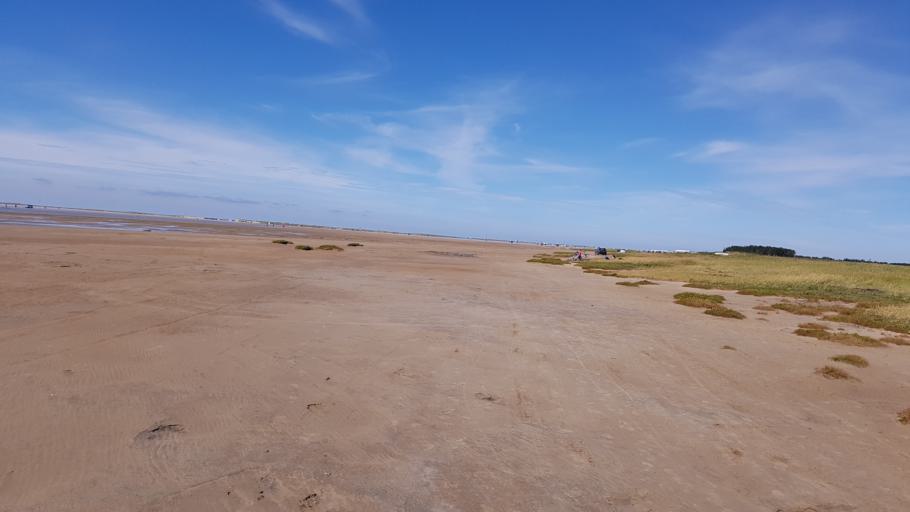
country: DE
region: Schleswig-Holstein
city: List
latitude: 55.0750
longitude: 8.5364
